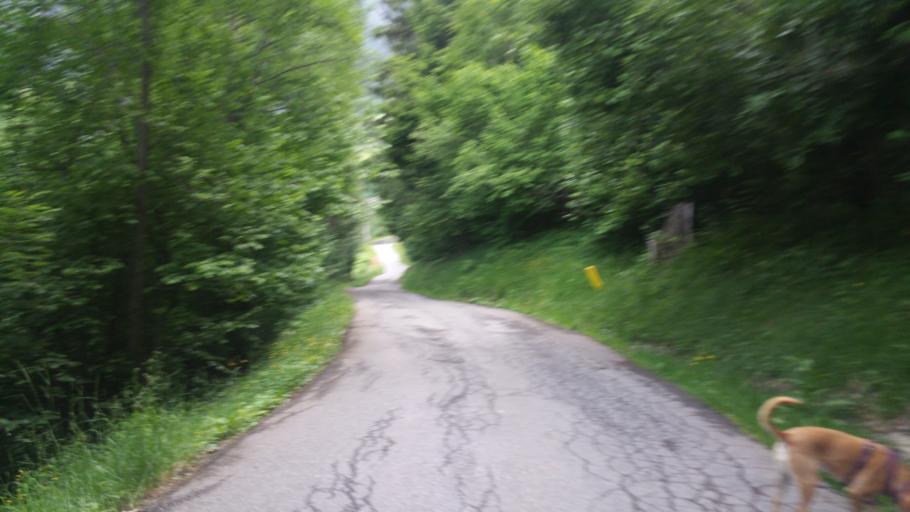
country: FR
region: Rhone-Alpes
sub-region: Departement de la Haute-Savoie
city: Les Houches
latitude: 45.8963
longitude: 6.7997
